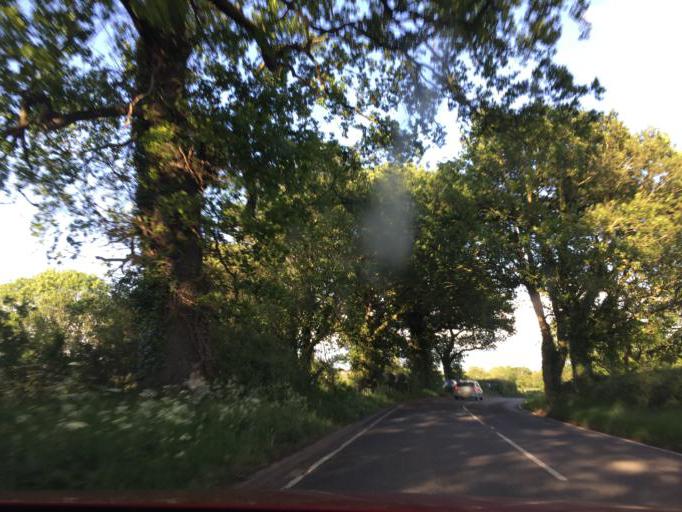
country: GB
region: England
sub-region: Warwickshire
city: Attleborough
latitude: 52.5002
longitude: -1.4562
